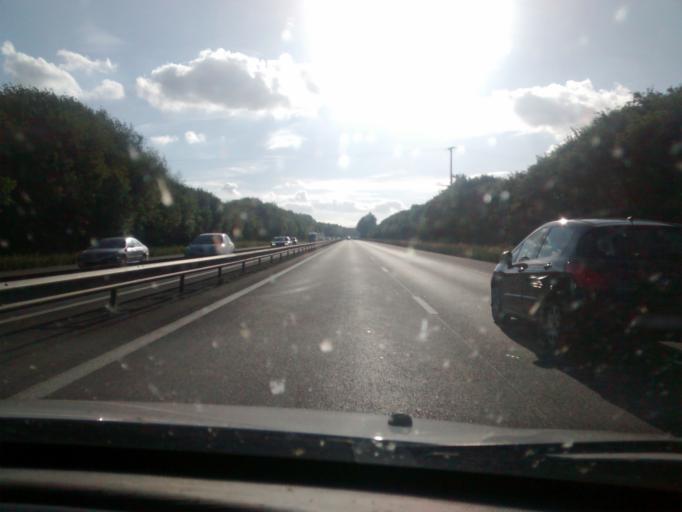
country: FR
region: Brittany
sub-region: Departement d'Ille-et-Vilaine
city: Torce
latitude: 48.0764
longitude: -1.2965
